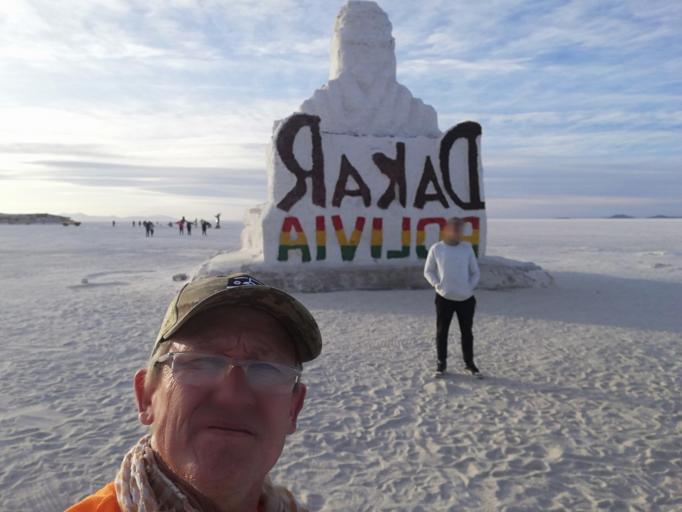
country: BO
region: Potosi
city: Colchani
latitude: -20.3299
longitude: -67.0449
